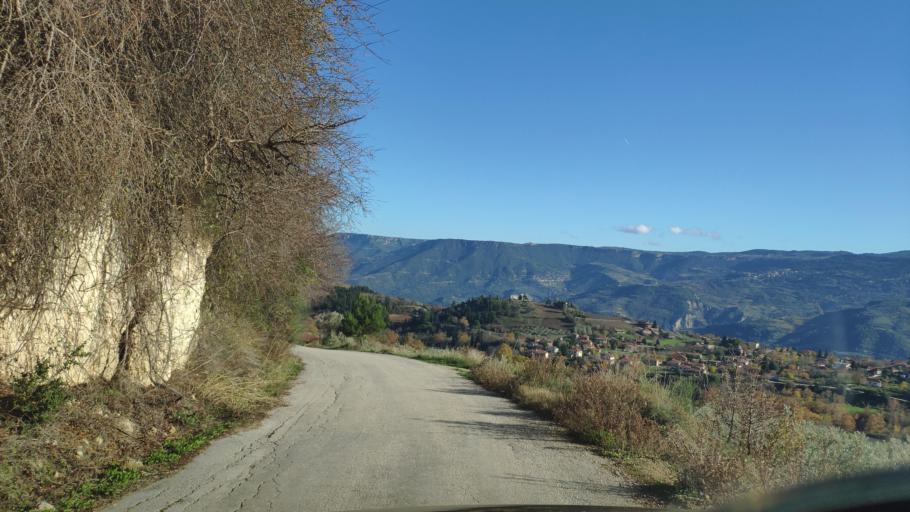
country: GR
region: Peloponnese
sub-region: Nomos Korinthias
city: Xylokastro
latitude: 38.0271
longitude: 22.4971
